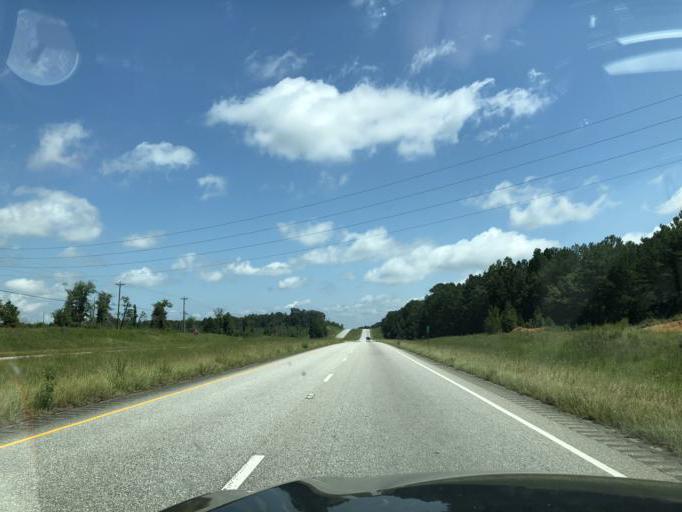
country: US
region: Alabama
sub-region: Barbour County
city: Eufaula
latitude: 31.7512
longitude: -85.2248
